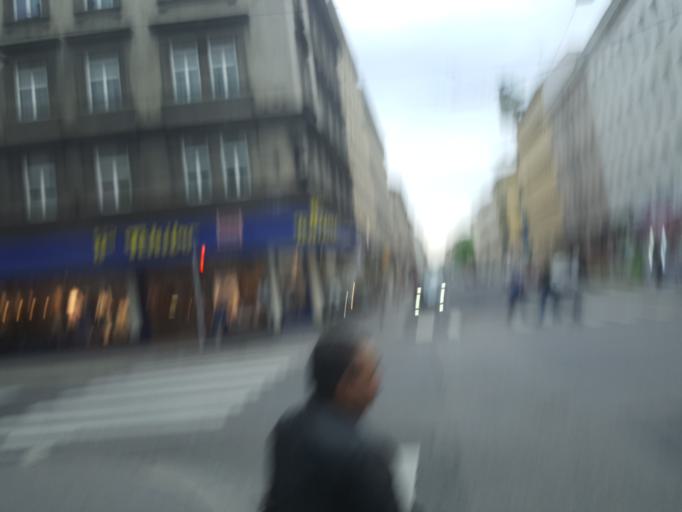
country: AT
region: Vienna
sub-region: Wien Stadt
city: Vienna
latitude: 48.1866
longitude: 16.3533
